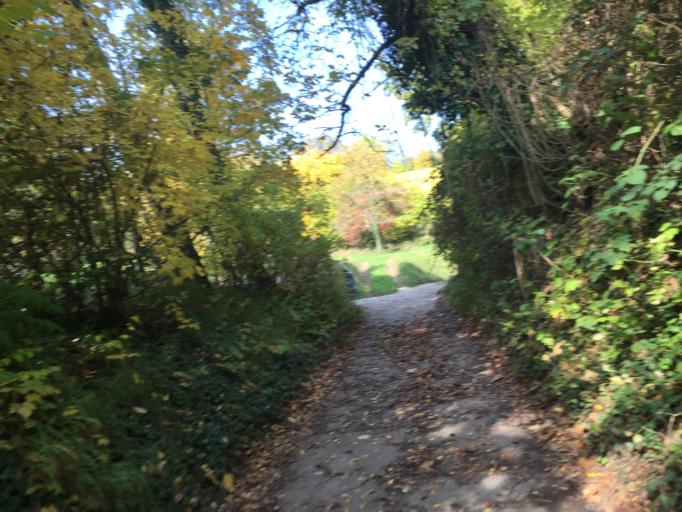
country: DE
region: Hesse
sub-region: Regierungsbezirk Darmstadt
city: Bensheim
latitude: 49.6776
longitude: 8.6387
